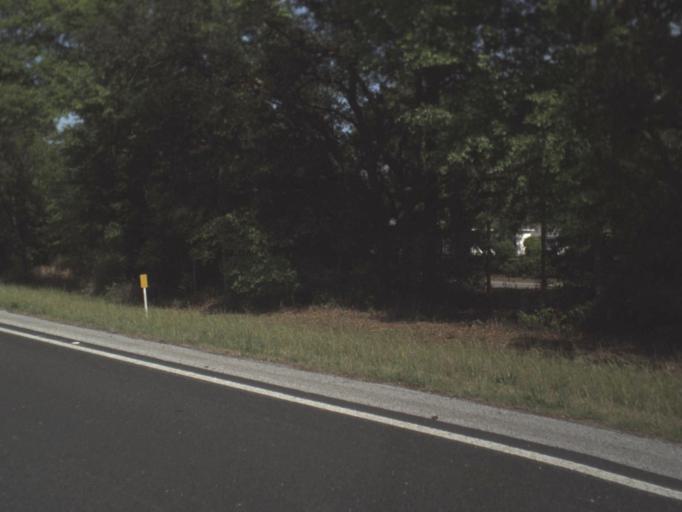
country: US
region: Florida
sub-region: Santa Rosa County
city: East Milton
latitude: 30.5949
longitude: -86.9988
